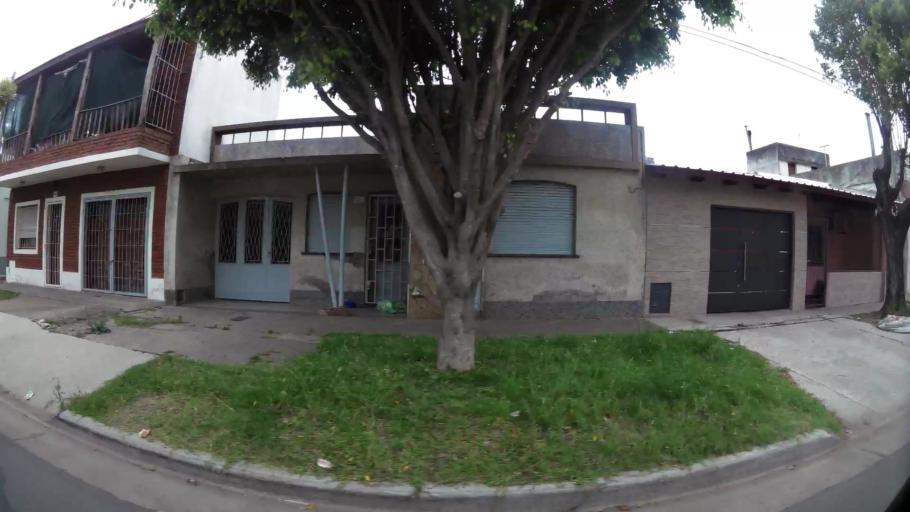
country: AR
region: Santa Fe
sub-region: Departamento de Rosario
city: Rosario
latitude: -32.9871
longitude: -60.6599
